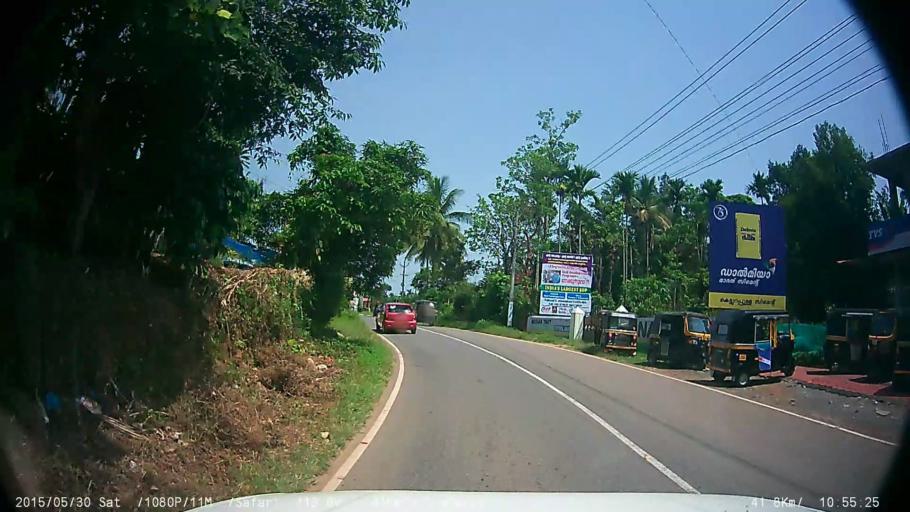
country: IN
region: Kerala
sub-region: Wayanad
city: Kalpetta
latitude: 11.6669
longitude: 76.0811
